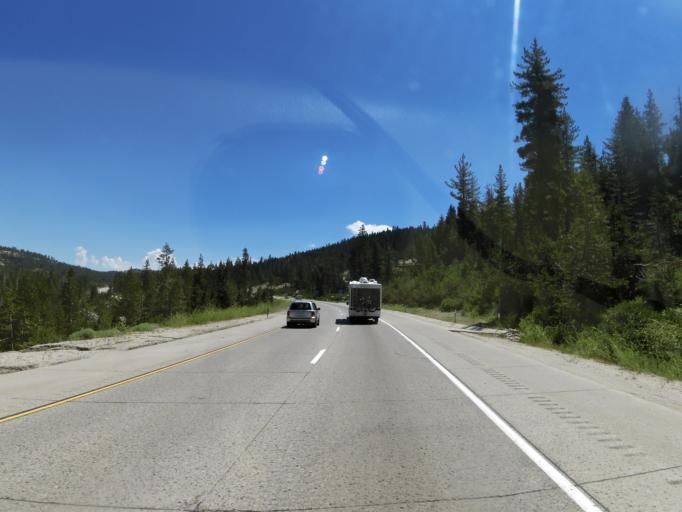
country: US
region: California
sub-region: Nevada County
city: Truckee
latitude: 39.3224
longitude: -120.4085
